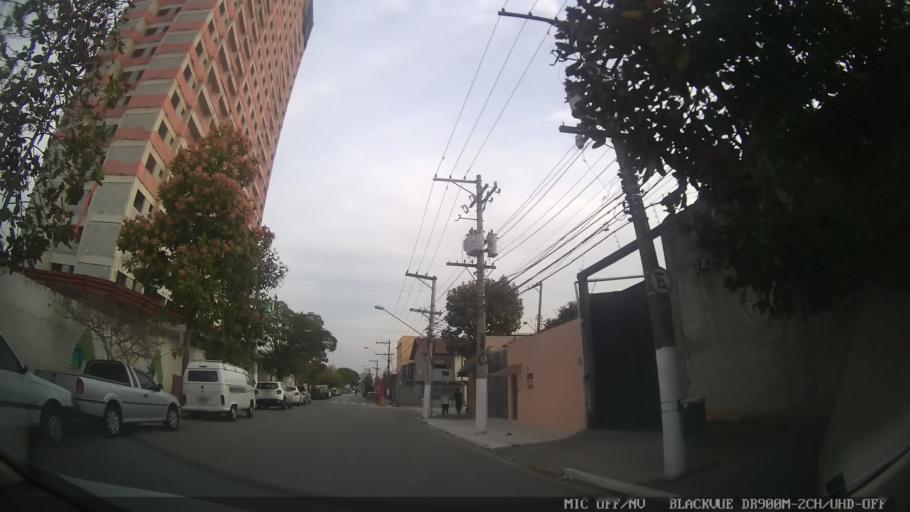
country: BR
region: Sao Paulo
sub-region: Sao Caetano Do Sul
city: Sao Caetano do Sul
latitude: -23.5919
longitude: -46.5951
